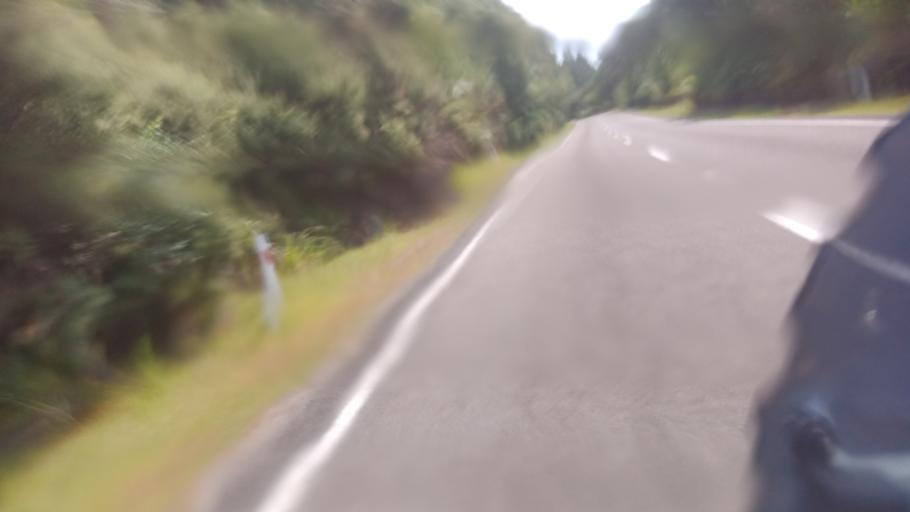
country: NZ
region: Bay of Plenty
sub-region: Opotiki District
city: Opotiki
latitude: -37.5764
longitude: 178.1076
